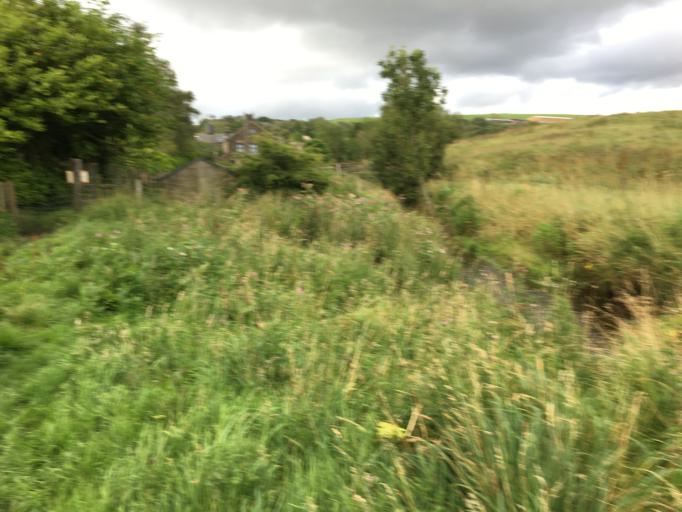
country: GB
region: England
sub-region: Borough of Oldham
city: Delph
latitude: 53.5873
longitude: -2.0413
